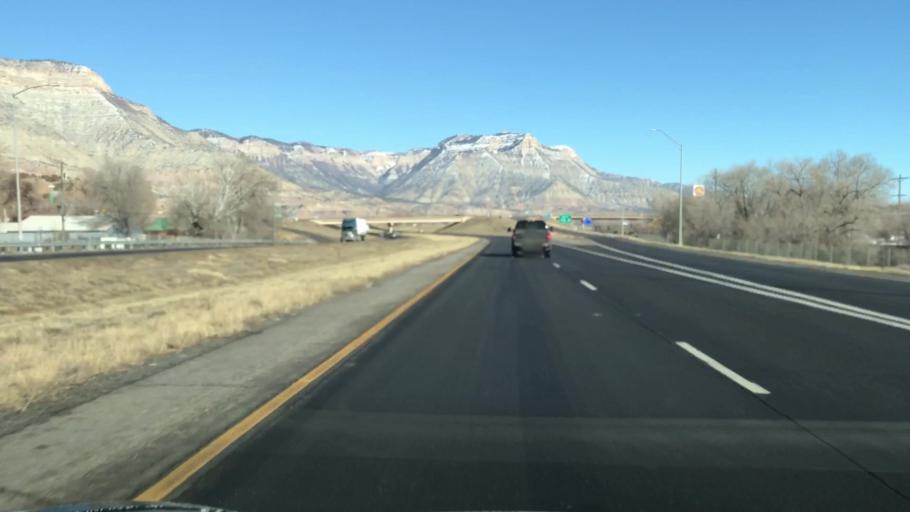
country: US
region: Colorado
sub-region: Garfield County
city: Parachute
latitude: 39.4524
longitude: -108.0508
